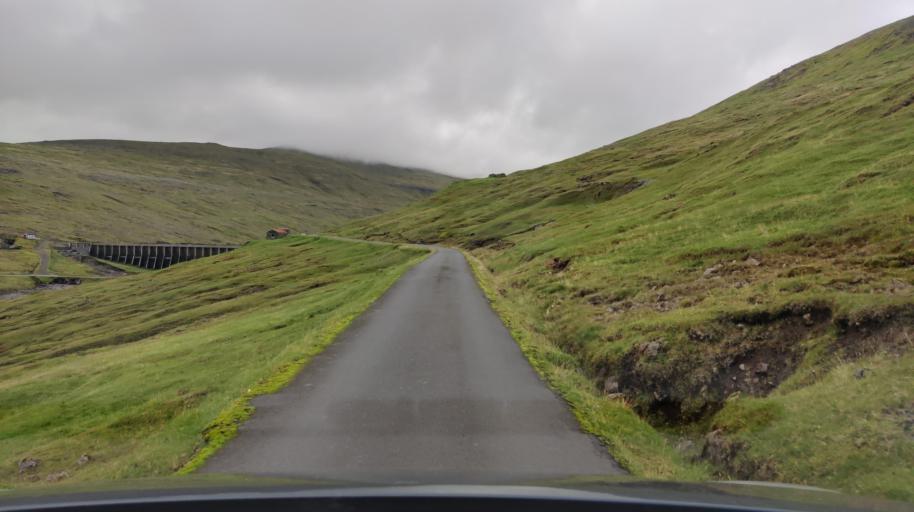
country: FO
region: Streymoy
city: Vestmanna
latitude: 62.1741
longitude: -7.1486
